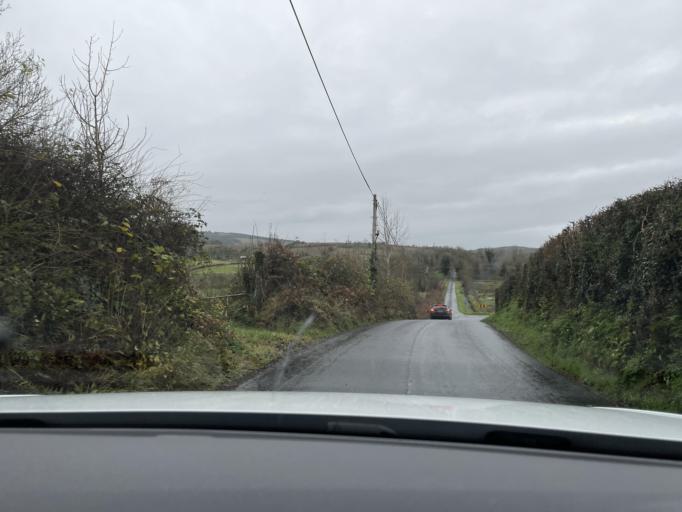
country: IE
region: Connaught
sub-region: County Leitrim
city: Manorhamilton
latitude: 54.2580
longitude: -8.2411
